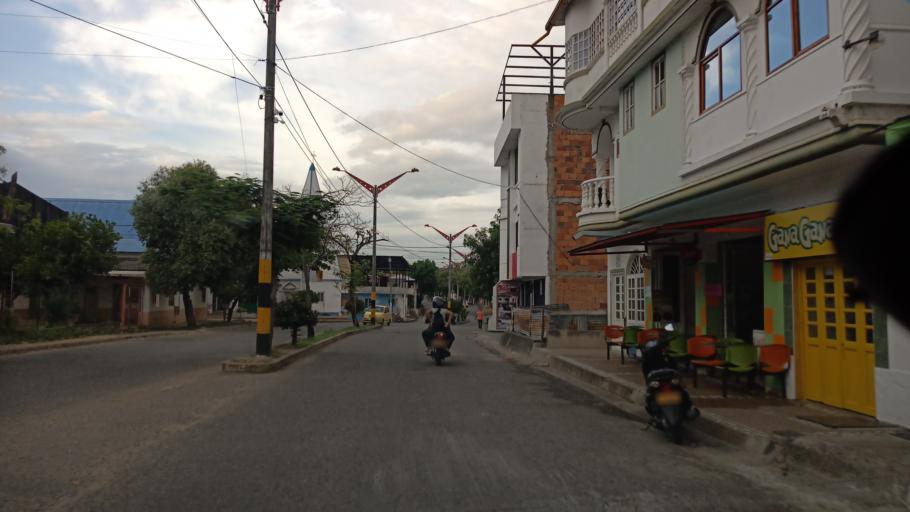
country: CO
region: Tolima
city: Melgar
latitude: 4.2007
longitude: -74.6492
